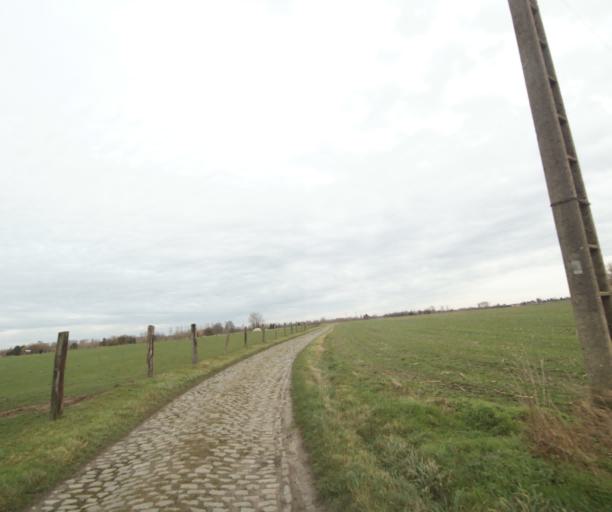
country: FR
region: Nord-Pas-de-Calais
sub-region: Departement du Nord
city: Hergnies
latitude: 50.4871
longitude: 3.5267
